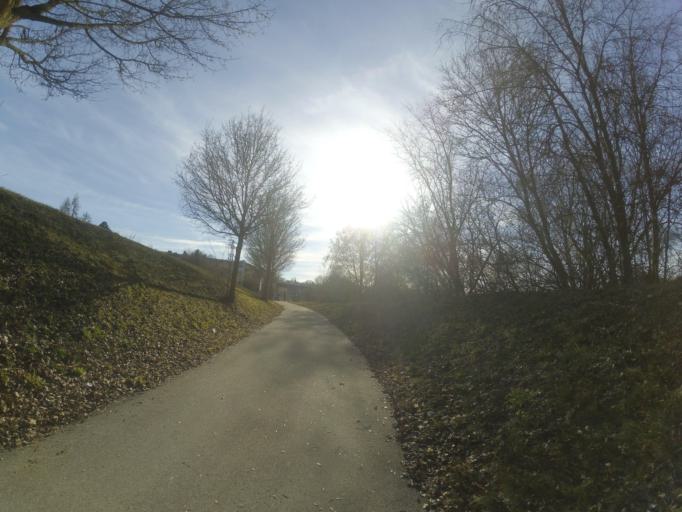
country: DE
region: Baden-Wuerttemberg
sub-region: Regierungsbezirk Stuttgart
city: Herbrechtingen
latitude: 48.6269
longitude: 10.1878
